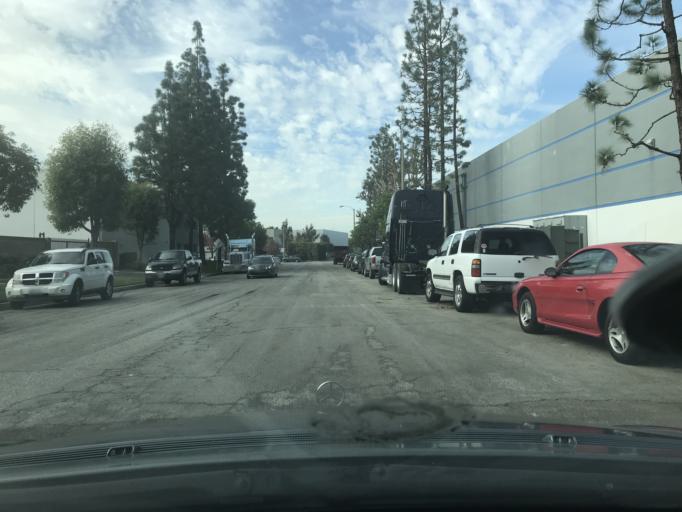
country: US
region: California
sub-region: Los Angeles County
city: Santa Fe Springs
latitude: 33.9460
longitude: -118.0754
